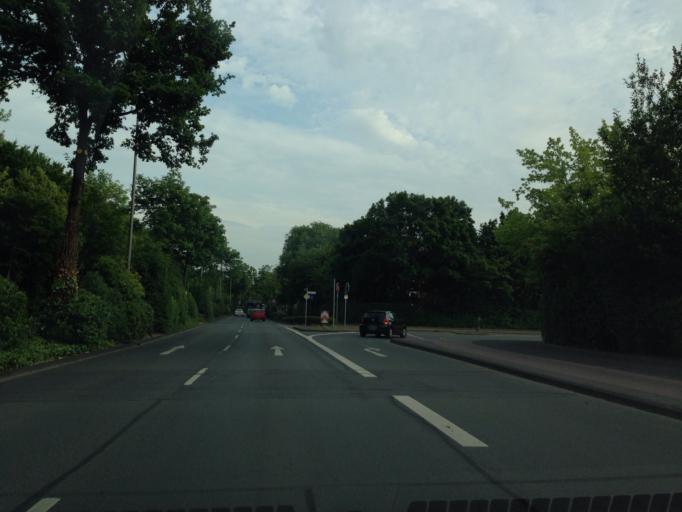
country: DE
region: North Rhine-Westphalia
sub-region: Regierungsbezirk Munster
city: Muenster
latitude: 51.9640
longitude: 7.6016
